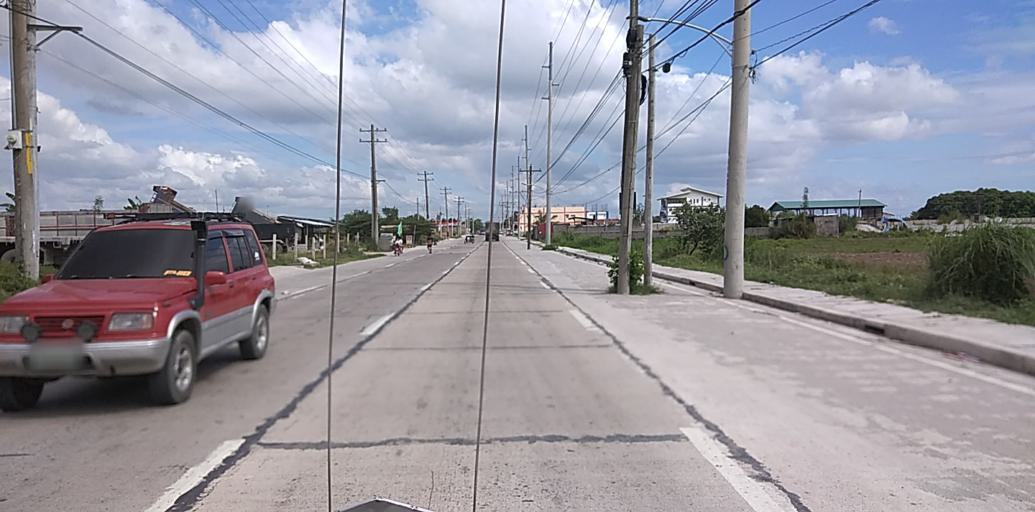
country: PH
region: Central Luzon
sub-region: Province of Pampanga
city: Porac
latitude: 15.0575
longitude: 120.5384
